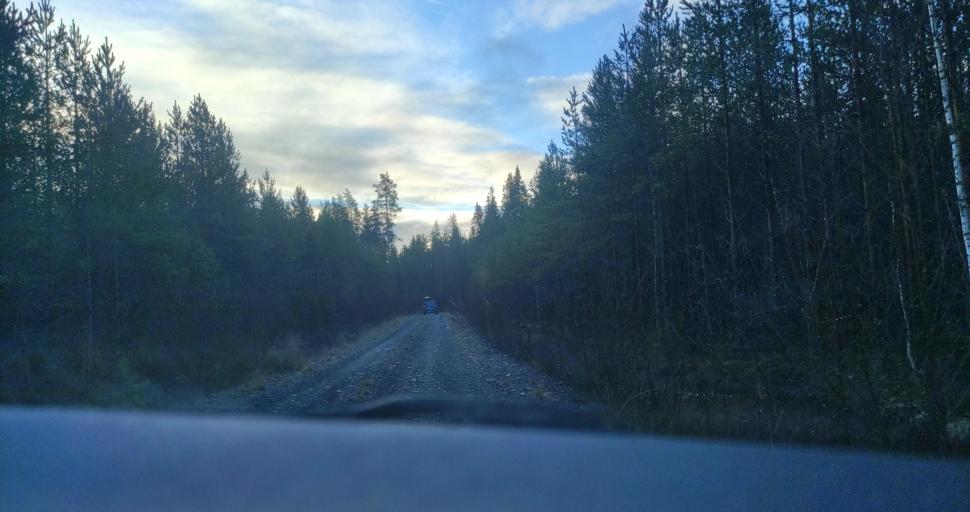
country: RU
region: Republic of Karelia
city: Pitkyaranta
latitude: 61.7361
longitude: 31.3648
